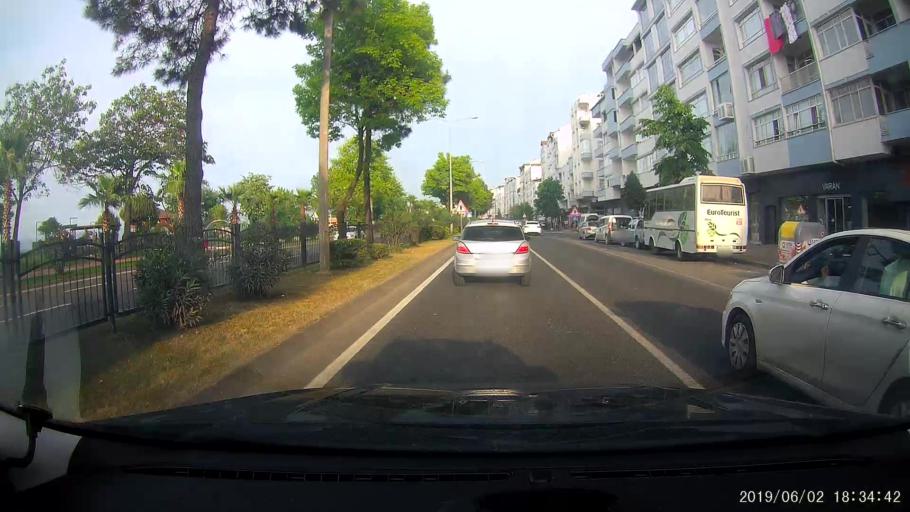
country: TR
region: Ordu
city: Fatsa
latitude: 41.0284
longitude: 37.5072
